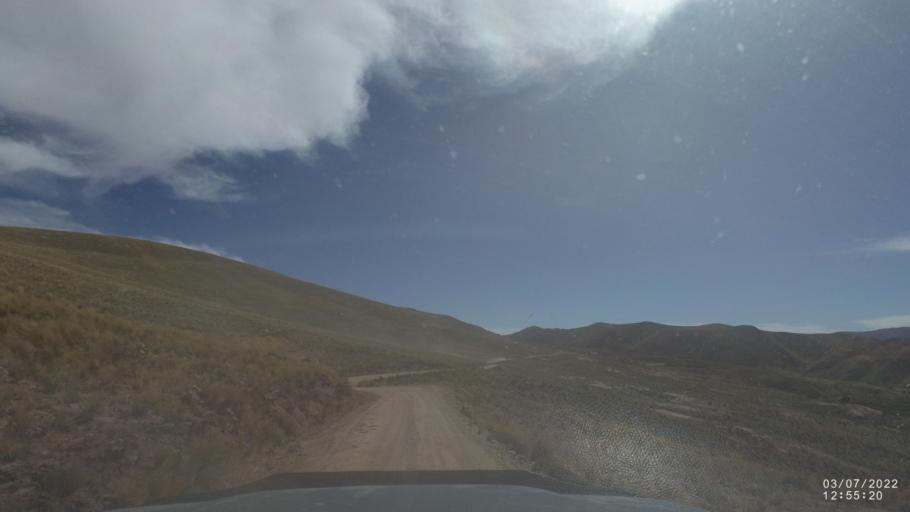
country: BO
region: Cochabamba
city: Sipe Sipe
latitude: -17.7338
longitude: -66.6695
